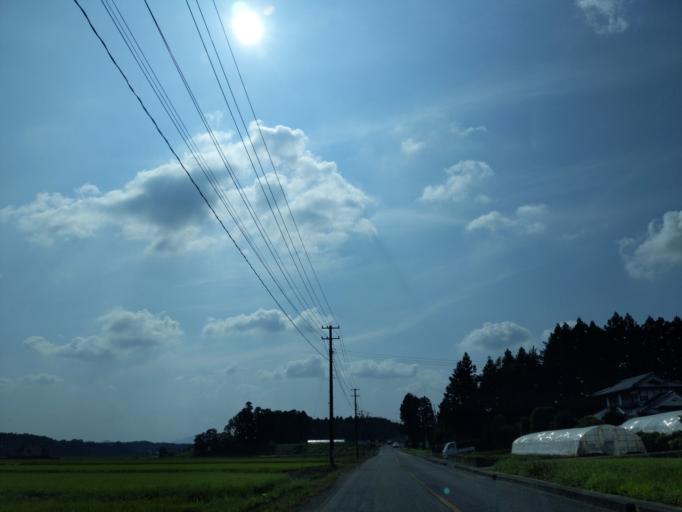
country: JP
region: Fukushima
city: Sukagawa
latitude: 37.3139
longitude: 140.3051
